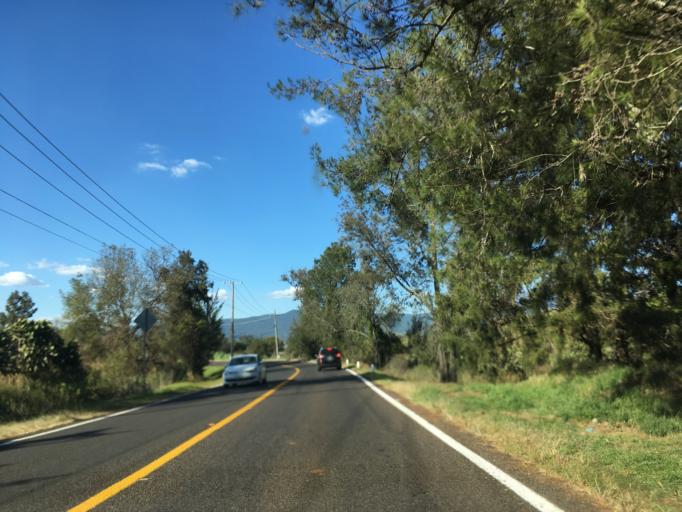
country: MX
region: Michoacan
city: Tzintzuntzan
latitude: 19.6187
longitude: -101.5767
